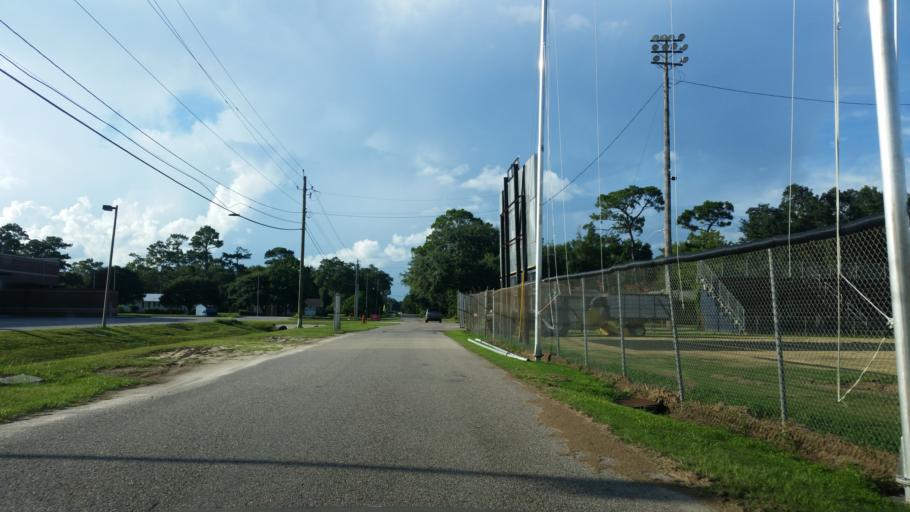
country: US
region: Alabama
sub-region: Baldwin County
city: Foley
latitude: 30.4092
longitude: -87.6895
